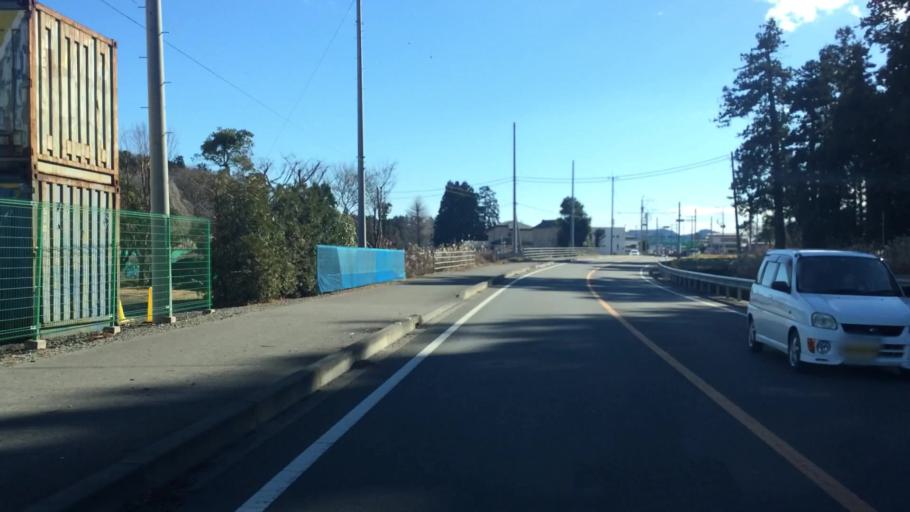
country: JP
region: Tochigi
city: Imaichi
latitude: 36.6984
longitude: 139.7548
